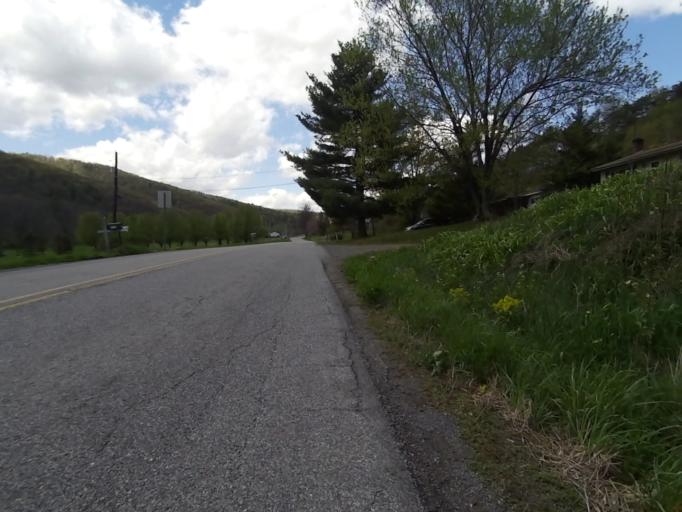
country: US
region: Pennsylvania
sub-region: Centre County
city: Milesburg
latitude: 40.9218
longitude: -77.8646
